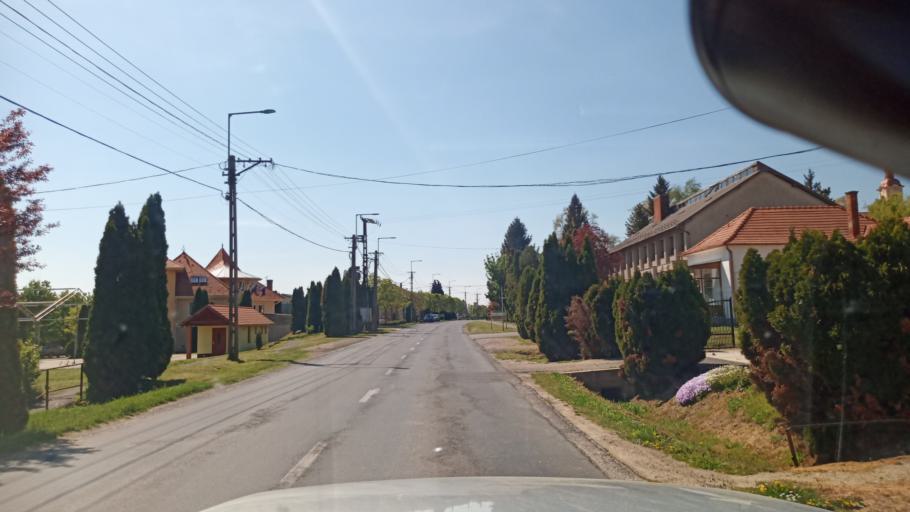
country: HU
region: Zala
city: Sarmellek
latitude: 46.7400
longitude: 17.1065
